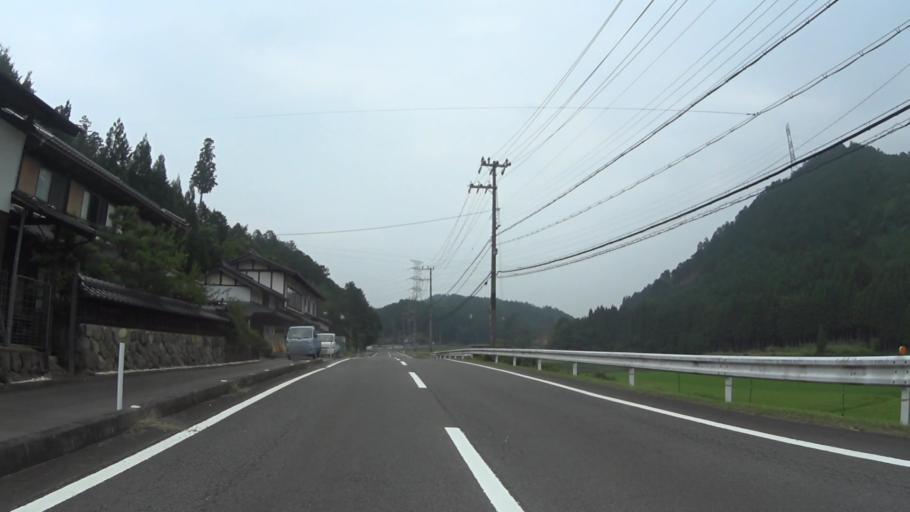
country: JP
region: Kyoto
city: Kameoka
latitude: 35.1700
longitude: 135.6103
